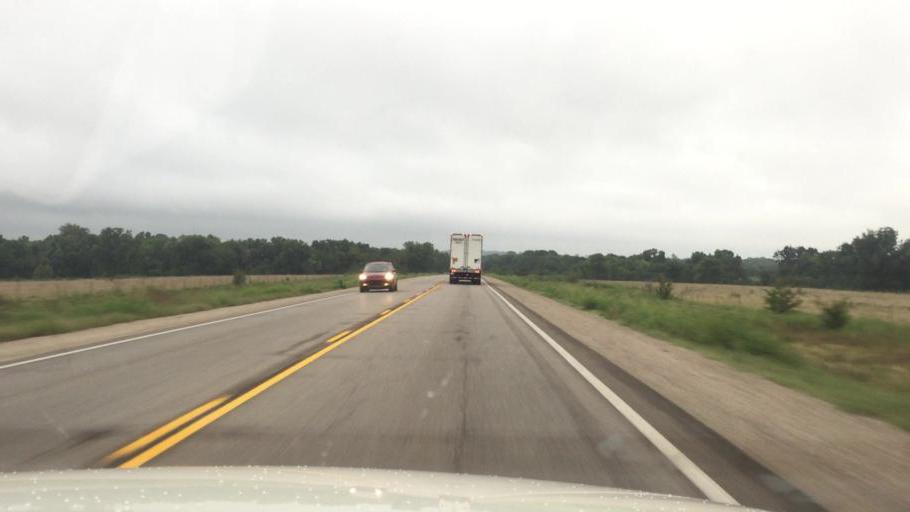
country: US
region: Kansas
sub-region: Montgomery County
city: Cherryvale
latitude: 37.1907
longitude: -95.5803
